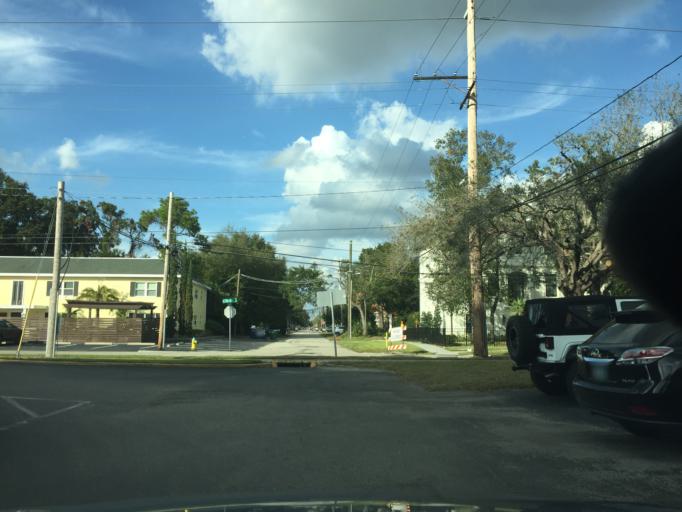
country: US
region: Florida
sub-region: Hillsborough County
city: Tampa
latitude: 27.9396
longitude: -82.4913
